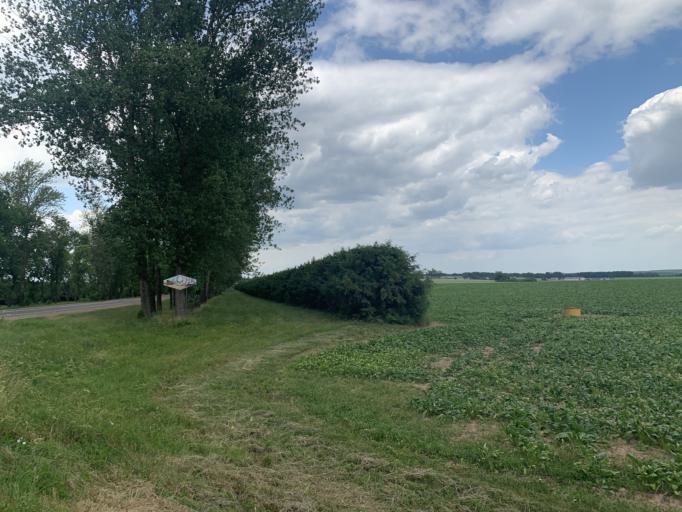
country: BY
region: Minsk
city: Nyasvizh
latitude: 53.2052
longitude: 26.7114
